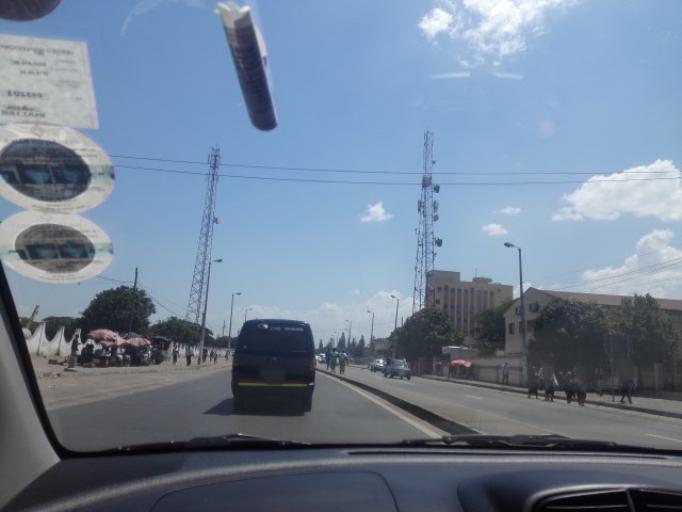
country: MZ
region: Maputo City
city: Maputo
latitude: -25.9354
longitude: 32.5496
